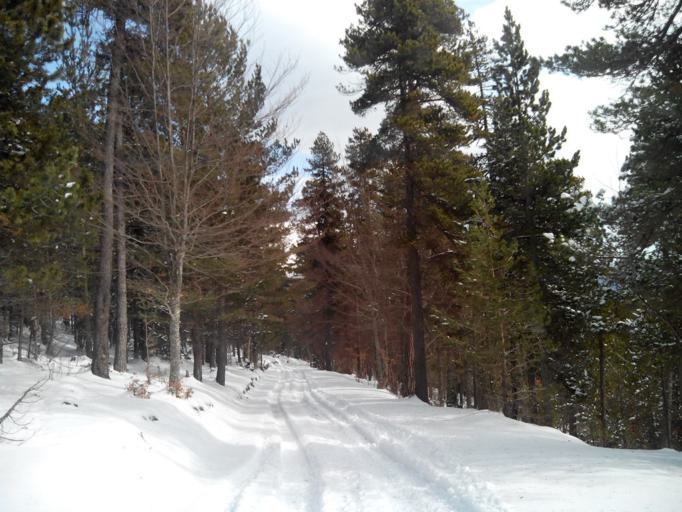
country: ES
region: Catalonia
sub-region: Provincia de Barcelona
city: Sant Julia de Cerdanyola
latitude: 42.2057
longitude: 1.9446
